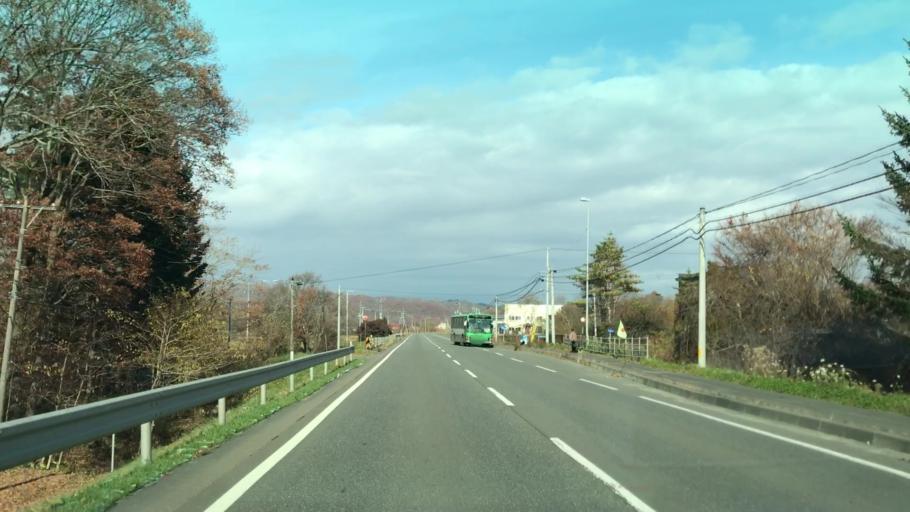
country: JP
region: Hokkaido
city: Shizunai-furukawacho
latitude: 42.6010
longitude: 142.1491
